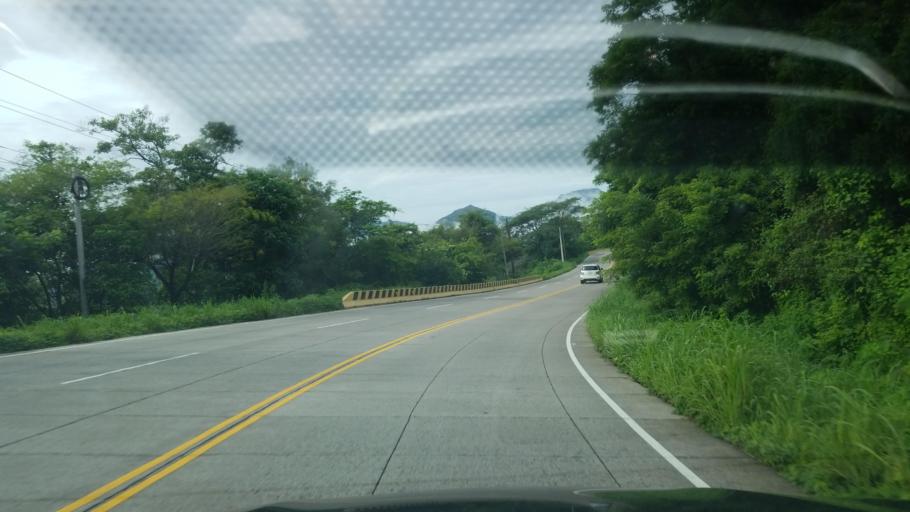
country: HN
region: Francisco Morazan
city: El Porvenir
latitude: 13.7155
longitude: -87.3168
